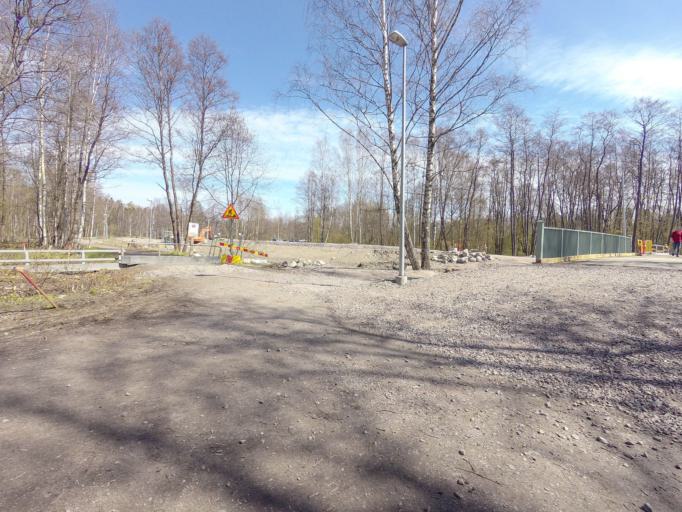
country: FI
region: Uusimaa
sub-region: Helsinki
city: Vantaa
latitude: 60.2207
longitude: 25.1240
